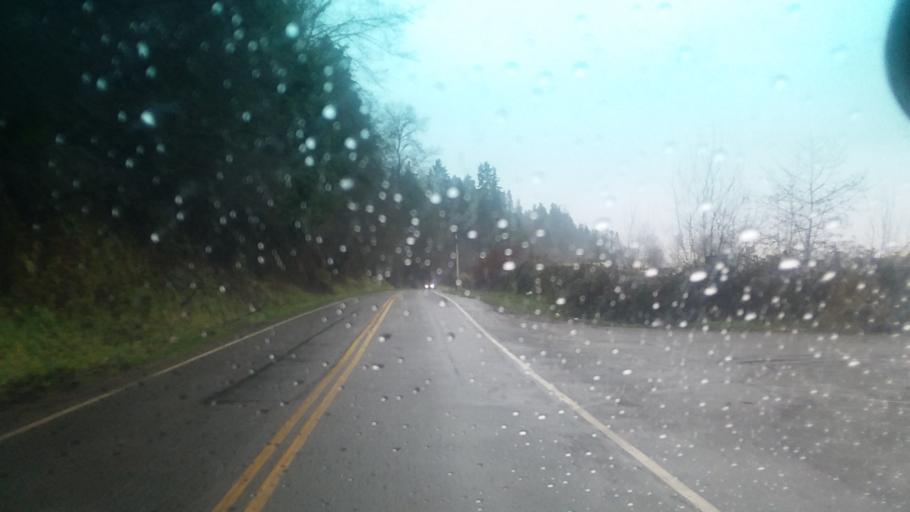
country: US
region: Washington
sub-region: King County
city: Pacific
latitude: 47.2609
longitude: -122.2631
